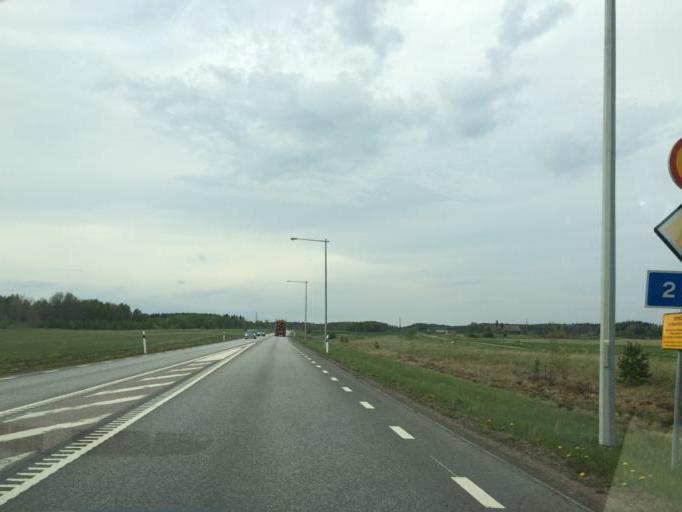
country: SE
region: Vaestmanland
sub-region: Kopings Kommun
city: Koping
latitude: 59.5279
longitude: 15.9604
